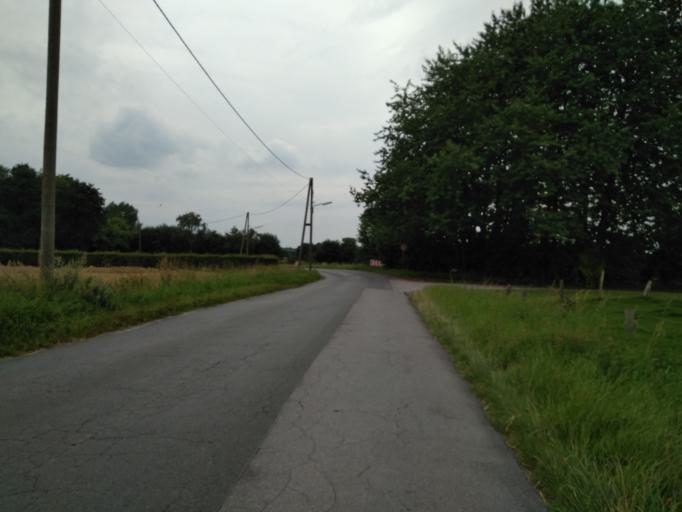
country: DE
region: North Rhine-Westphalia
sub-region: Regierungsbezirk Munster
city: Bottrop
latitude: 51.5987
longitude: 6.8991
